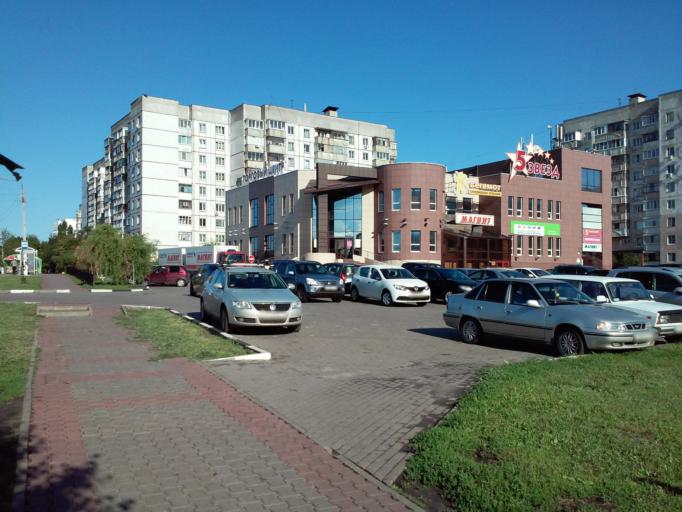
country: RU
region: Belgorod
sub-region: Belgorodskiy Rayon
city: Belgorod
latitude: 50.5549
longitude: 36.5724
